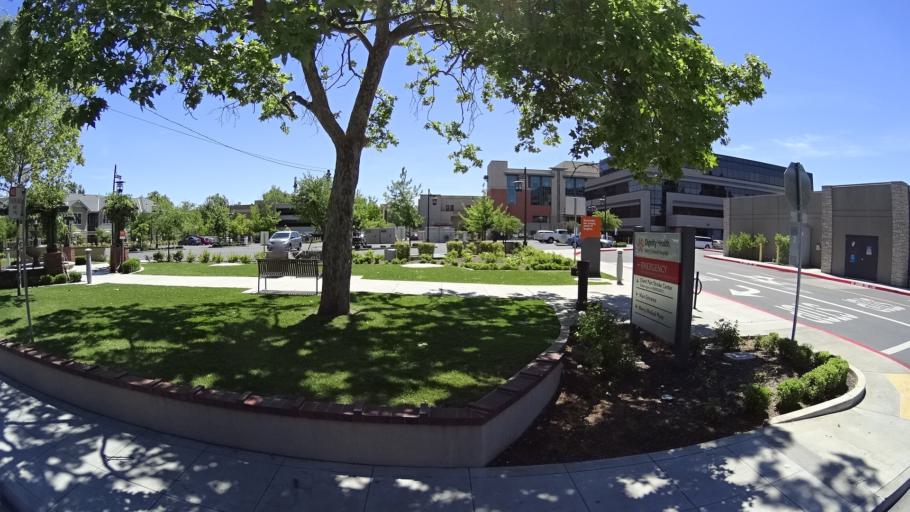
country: US
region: California
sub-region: Sacramento County
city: Sacramento
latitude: 38.5713
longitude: -121.4542
